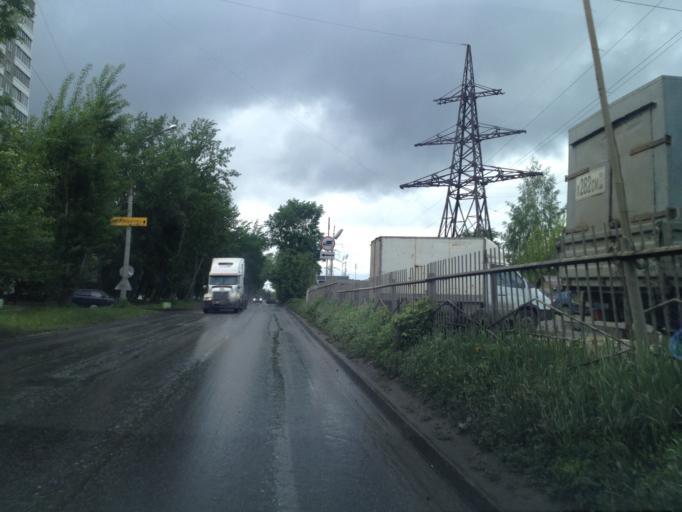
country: RU
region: Sverdlovsk
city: Yekaterinburg
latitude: 56.8724
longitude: 60.5595
